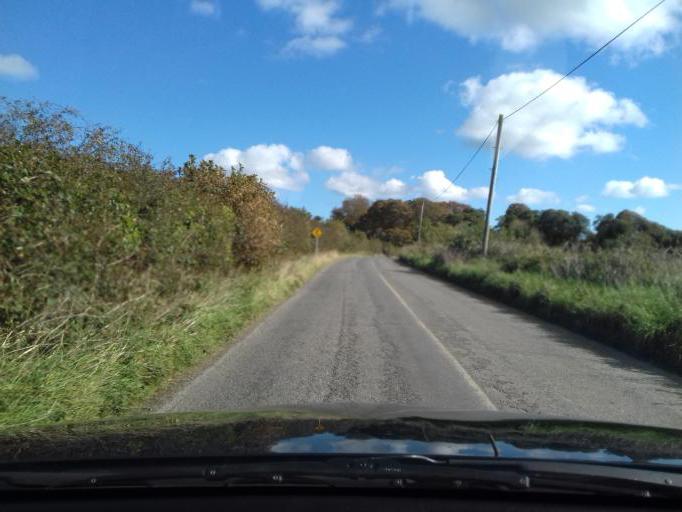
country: IE
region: Leinster
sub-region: An Mhi
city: Slane
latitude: 53.6860
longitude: -6.5369
